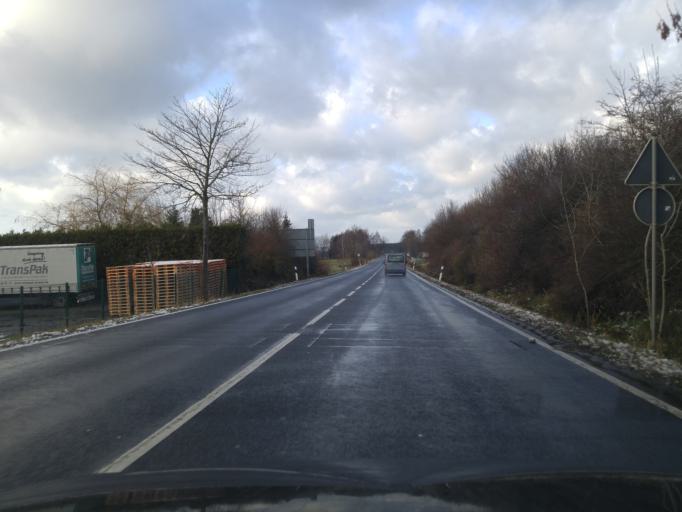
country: DE
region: Lower Saxony
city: Hannoversch Munden
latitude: 51.3737
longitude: 9.6297
